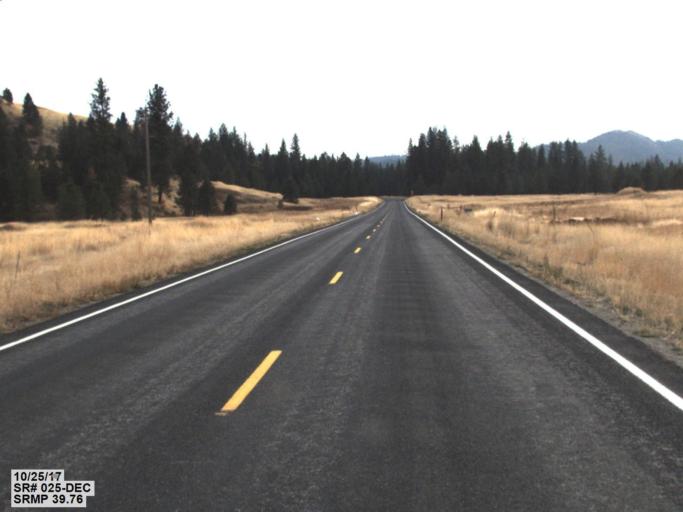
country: US
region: Washington
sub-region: Lincoln County
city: Davenport
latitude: 48.0939
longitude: -118.2026
